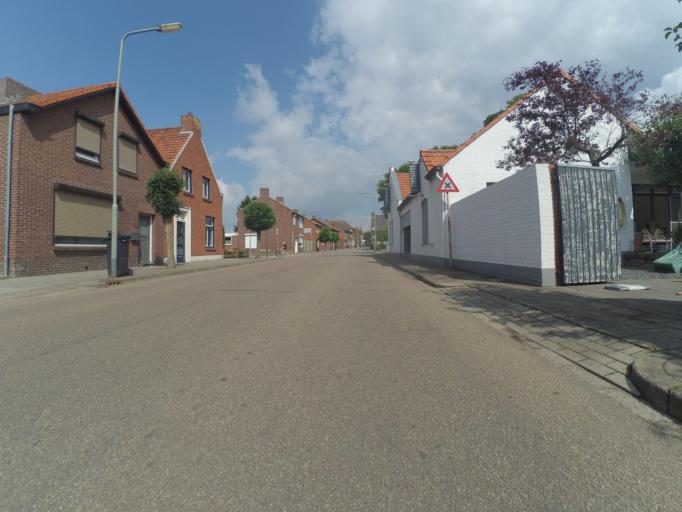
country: NL
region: Limburg
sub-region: Gemeente Roerdalen
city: Montfort
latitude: 51.1235
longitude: 5.9494
